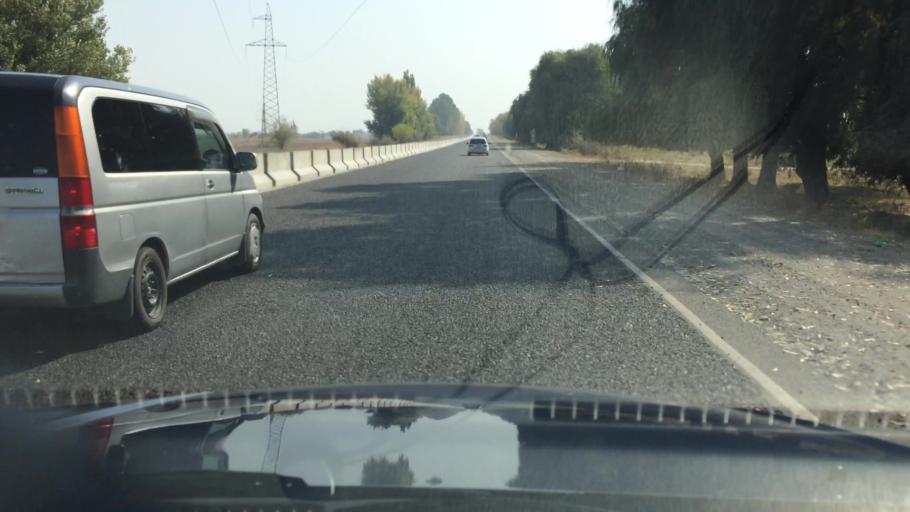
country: KG
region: Chuy
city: Kant
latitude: 42.9671
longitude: 74.9091
